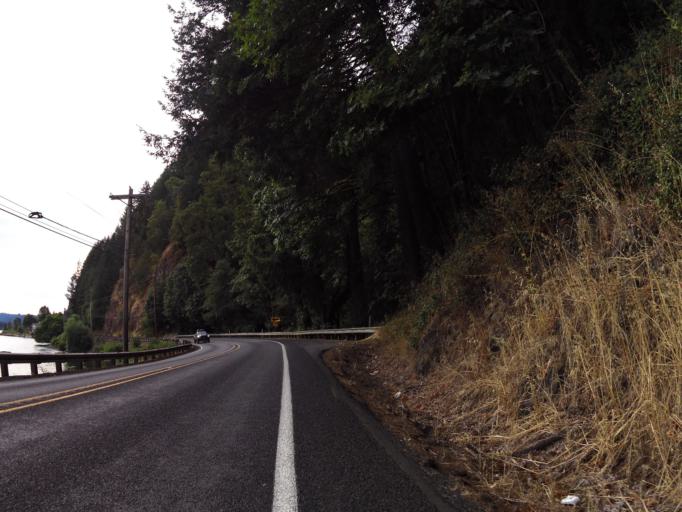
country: US
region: Washington
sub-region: Cowlitz County
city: West Longview
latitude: 46.1901
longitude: -123.1139
